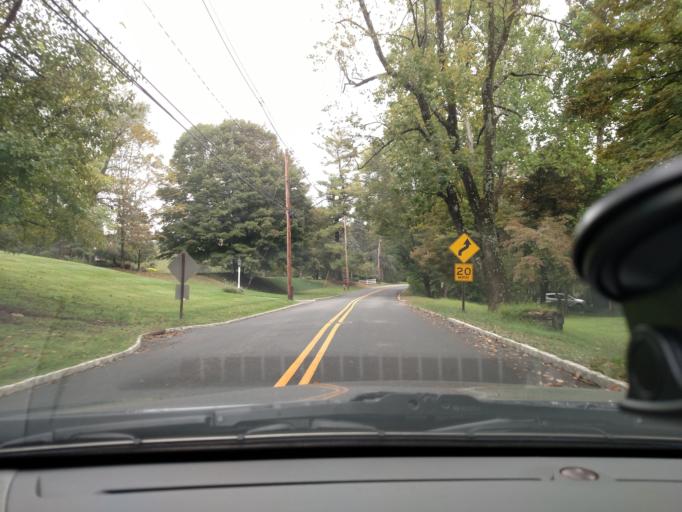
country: US
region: New Jersey
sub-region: Morris County
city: Mendham
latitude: 40.7954
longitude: -74.5633
